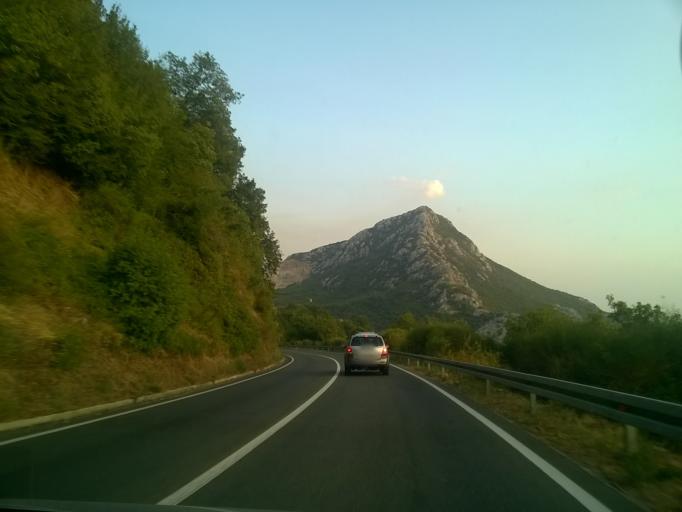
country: ME
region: Bar
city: Sutomore
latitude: 42.1715
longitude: 19.0086
